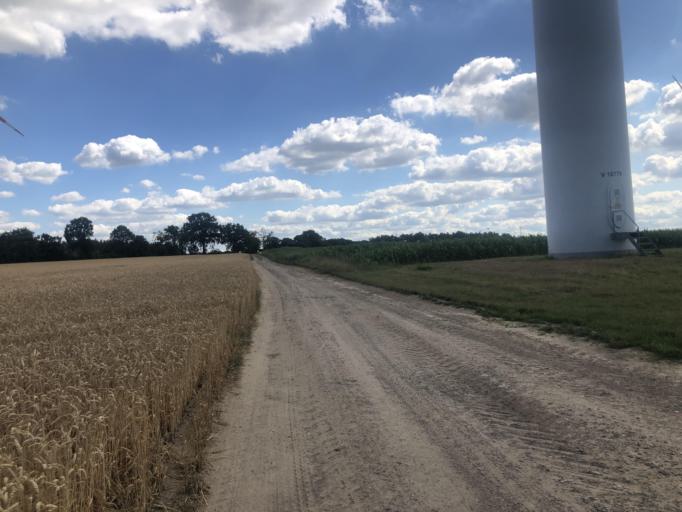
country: DE
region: Lower Saxony
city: Dahlem
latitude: 53.2266
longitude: 10.7701
